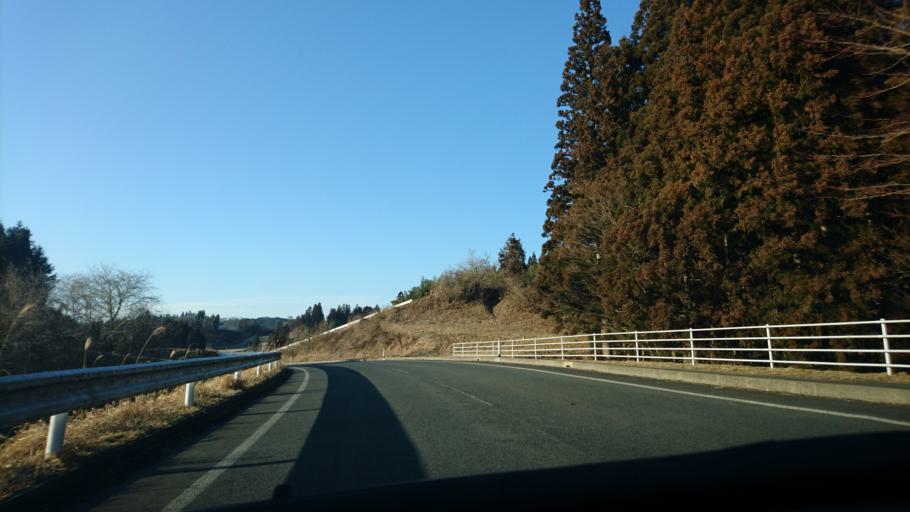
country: JP
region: Iwate
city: Ichinoseki
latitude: 38.9049
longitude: 141.3877
